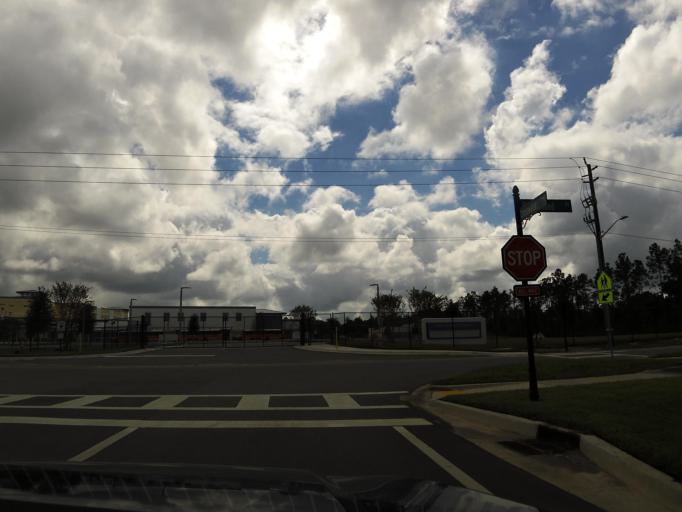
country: US
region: Florida
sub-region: Saint Johns County
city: Palm Valley
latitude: 30.0513
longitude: -81.3961
